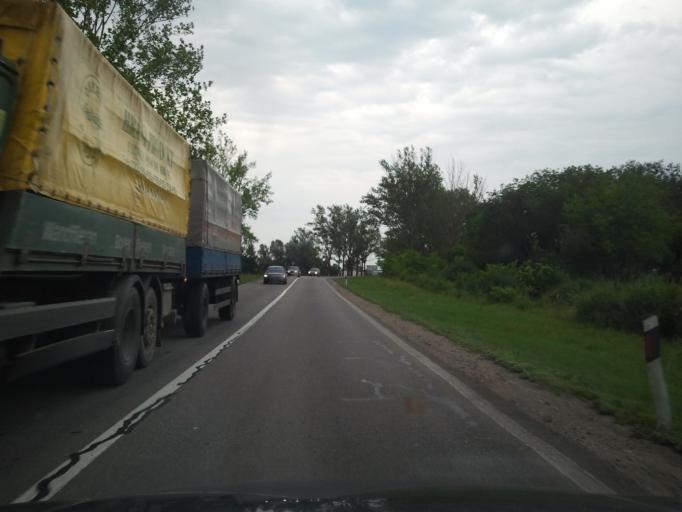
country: RS
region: Autonomna Pokrajina Vojvodina
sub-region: Sremski Okrug
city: Ruma
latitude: 44.9731
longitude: 19.8097
